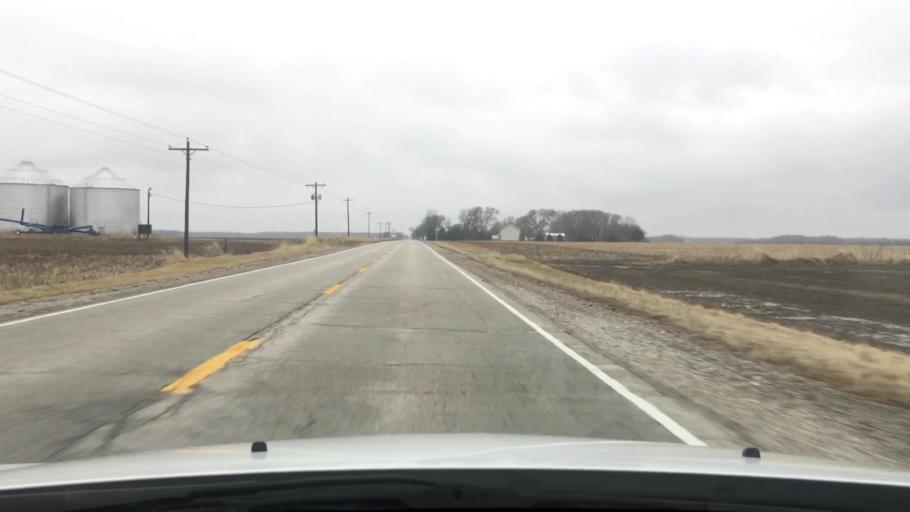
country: US
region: Illinois
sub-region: Iroquois County
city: Watseka
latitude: 40.8888
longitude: -87.7882
